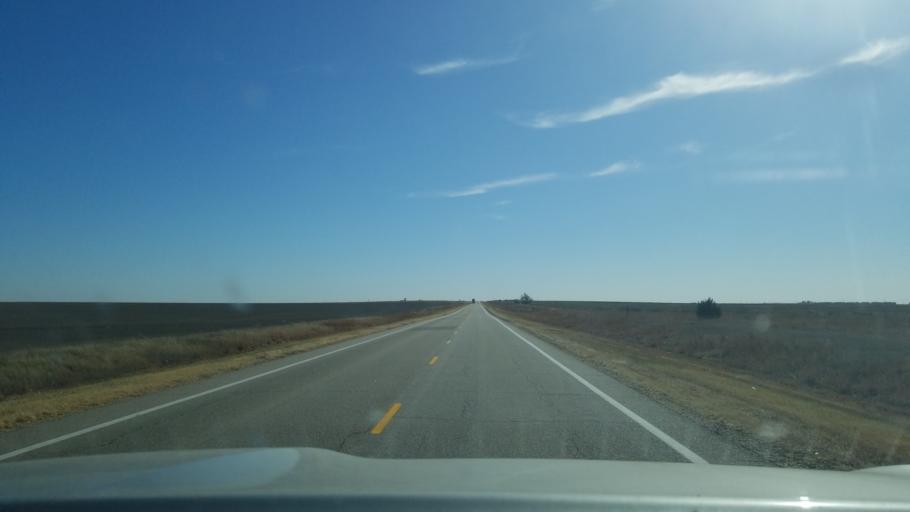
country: US
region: Kansas
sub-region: Ford County
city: Dodge City
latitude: 37.5842
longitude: -99.6806
